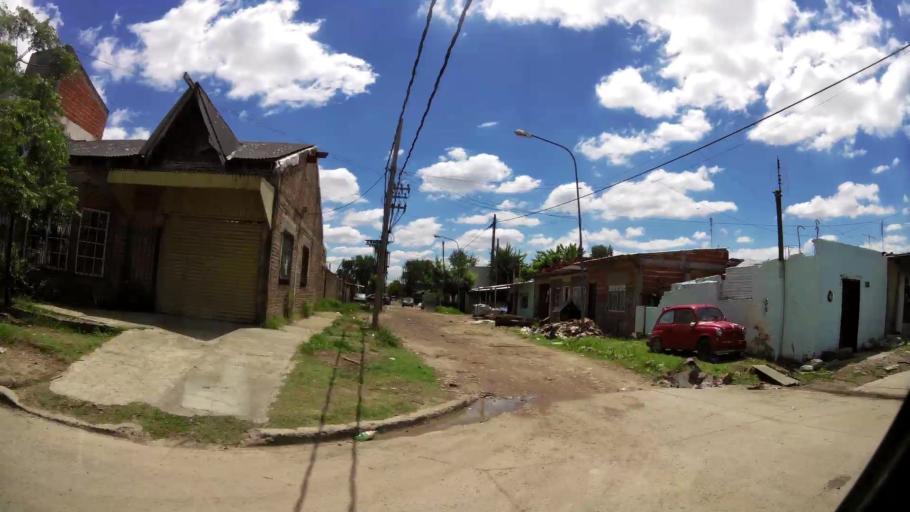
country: AR
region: Buenos Aires
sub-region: Partido de Lanus
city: Lanus
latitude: -34.7202
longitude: -58.4199
